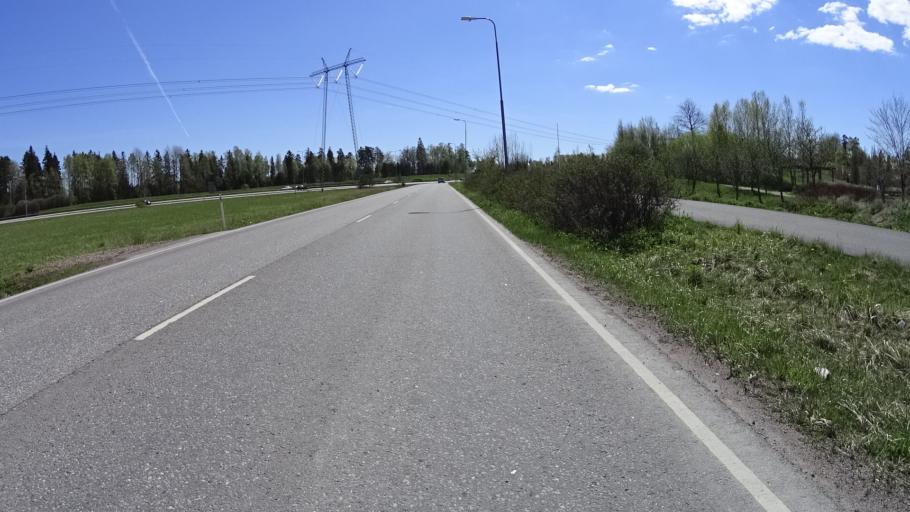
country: FI
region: Uusimaa
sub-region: Helsinki
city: Kauniainen
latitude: 60.2512
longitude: 24.7092
